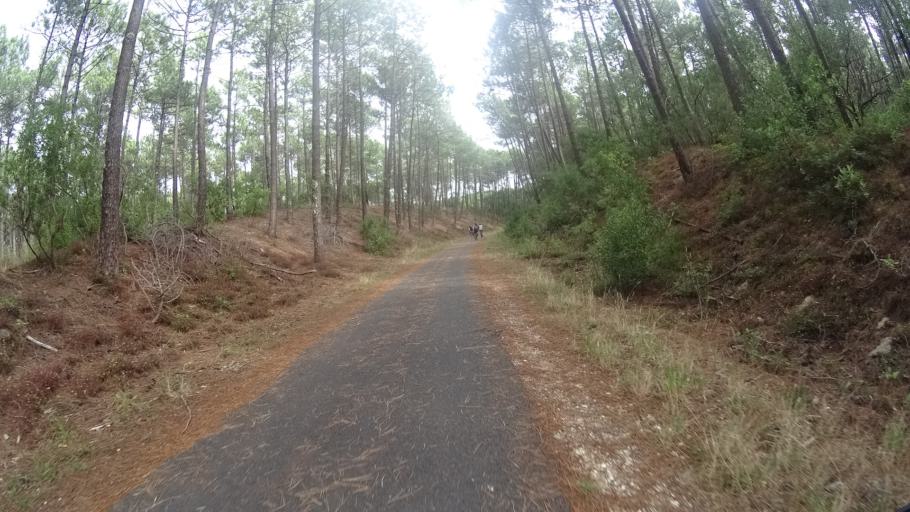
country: FR
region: Aquitaine
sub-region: Departement de la Gironde
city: Lacanau
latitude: 45.0061
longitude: -1.1400
